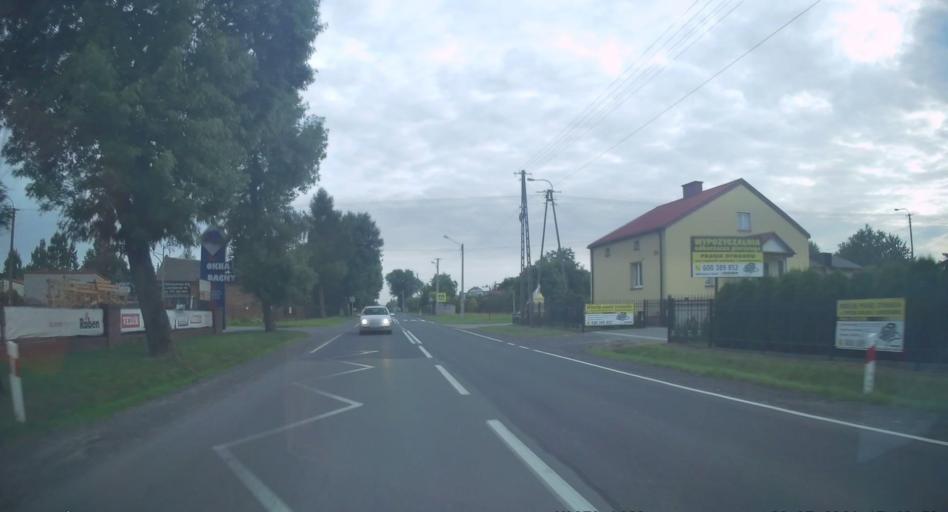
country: PL
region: Lodz Voivodeship
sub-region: Powiat radomszczanski
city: Radomsko
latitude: 51.1033
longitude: 19.4635
